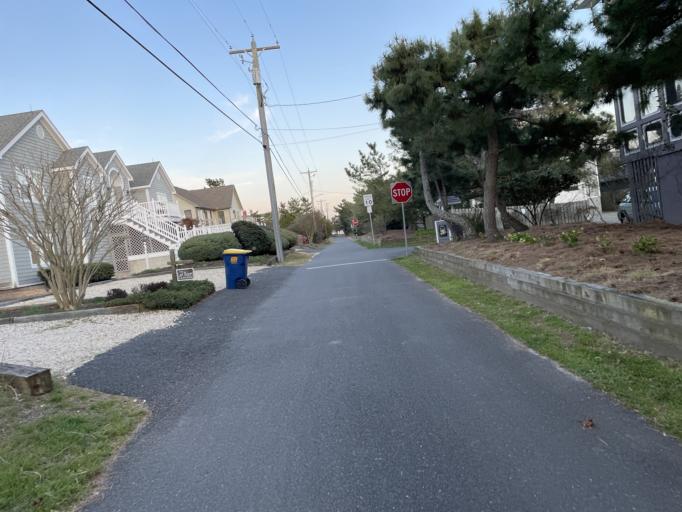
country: US
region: Delaware
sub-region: Sussex County
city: Lewes
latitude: 38.7874
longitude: -75.1542
